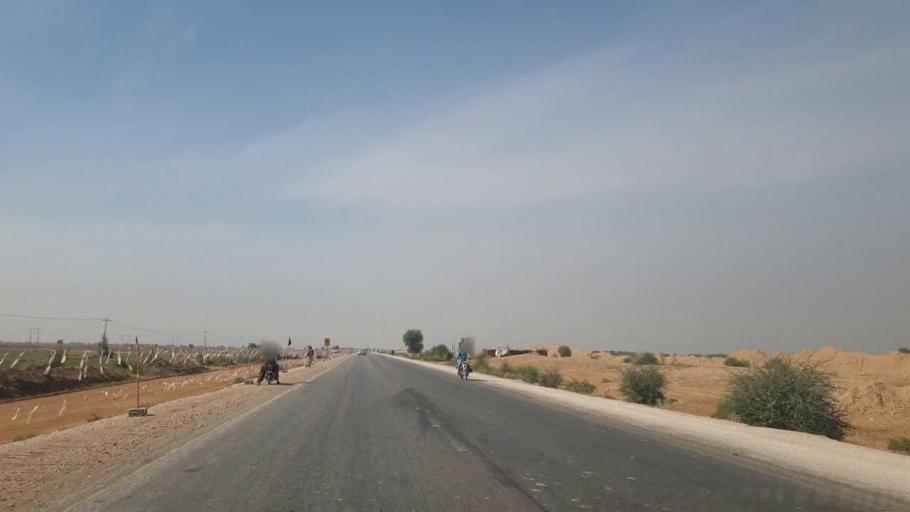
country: PK
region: Sindh
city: Sann
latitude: 26.0156
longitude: 68.1421
